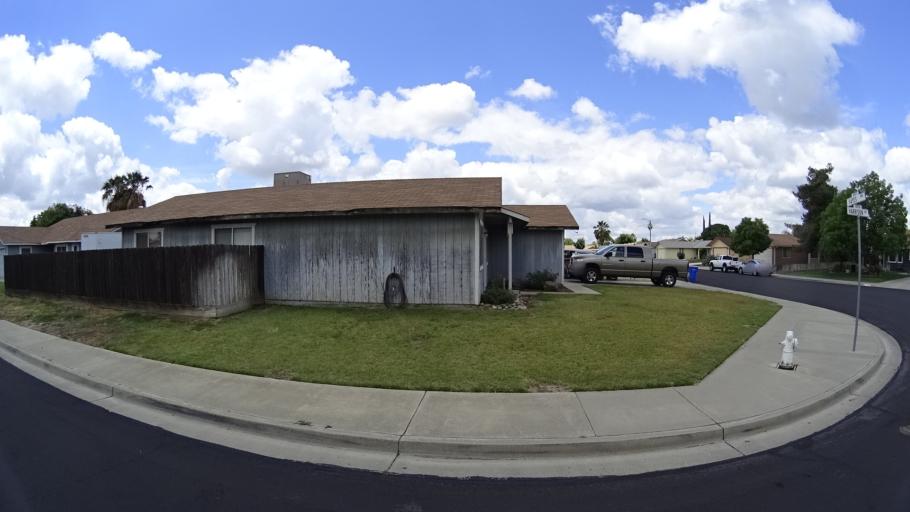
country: US
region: California
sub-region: Kings County
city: Hanford
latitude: 36.3457
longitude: -119.6285
